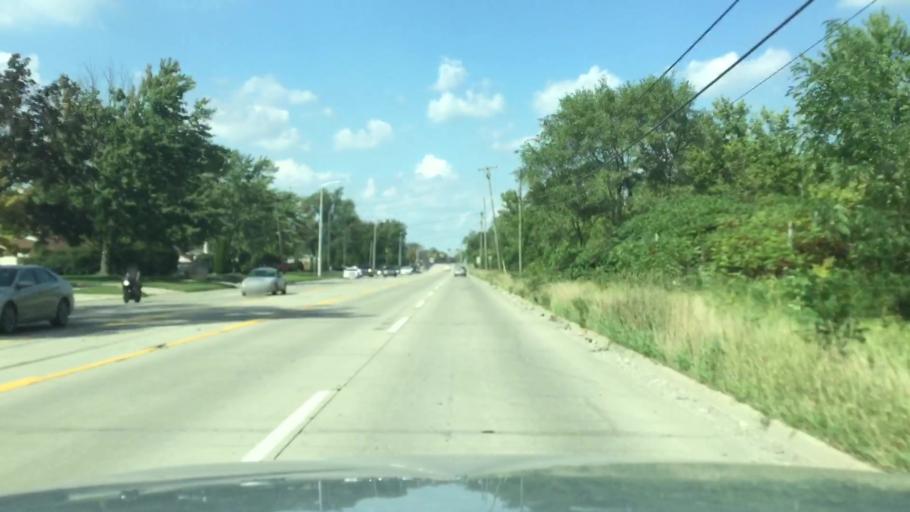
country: US
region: Michigan
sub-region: Wayne County
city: Wayne
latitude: 42.2806
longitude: -83.3484
